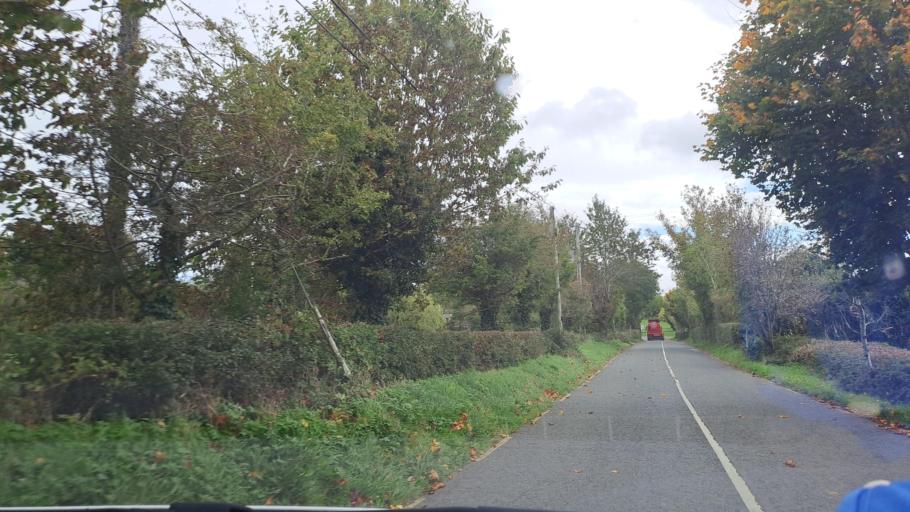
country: IE
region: Ulster
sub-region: An Cabhan
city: Kingscourt
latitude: 53.9385
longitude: -6.7825
